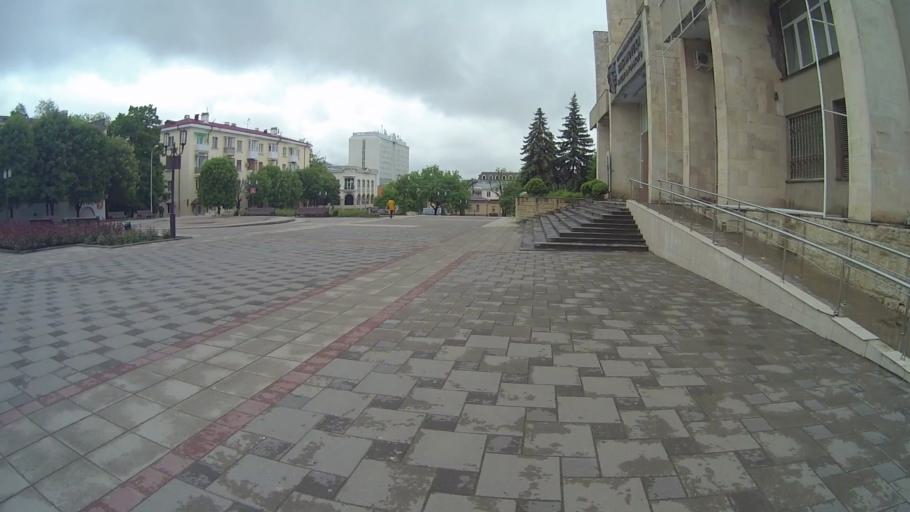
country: RU
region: Stavropol'skiy
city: Pyatigorsk
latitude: 44.0389
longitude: 43.0707
